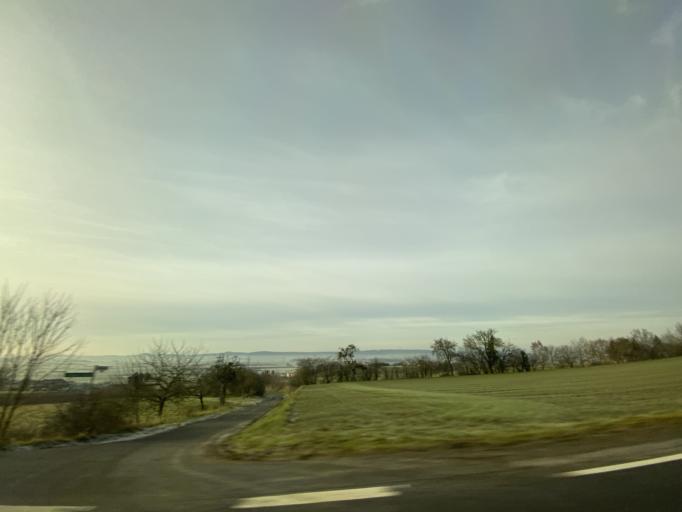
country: DE
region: Hesse
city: Amoneburg
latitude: 50.7946
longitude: 8.9179
